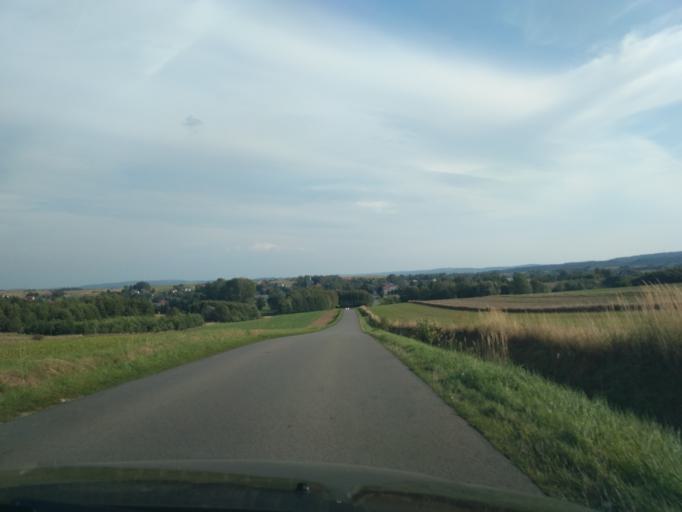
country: PL
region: Subcarpathian Voivodeship
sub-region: Powiat rzeszowski
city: Niechobrz
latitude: 50.0021
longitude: 21.8693
